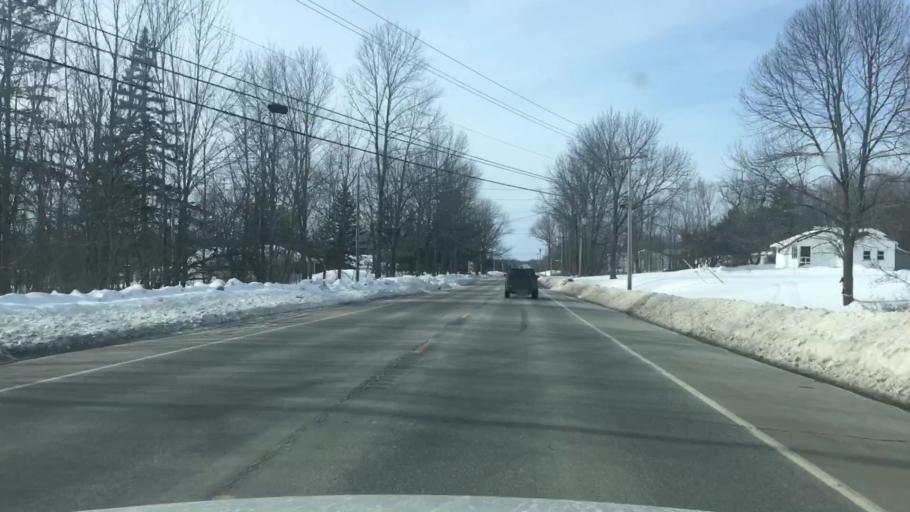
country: US
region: Maine
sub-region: Penobscot County
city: Kenduskeag
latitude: 44.9730
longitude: -68.9811
